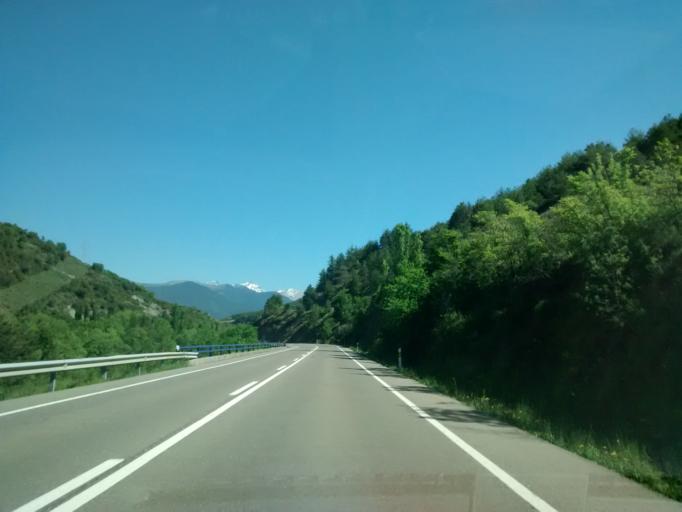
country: ES
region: Aragon
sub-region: Provincia de Huesca
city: Jaca
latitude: 42.5993
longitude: -0.5437
